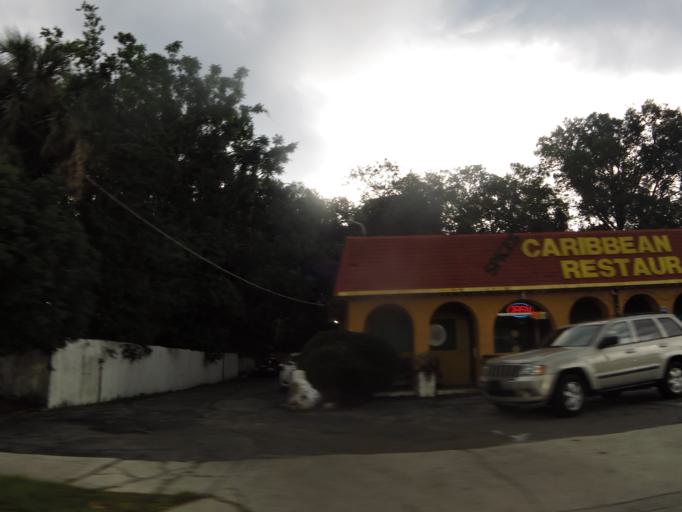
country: US
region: Florida
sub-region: Duval County
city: Jacksonville
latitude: 30.3342
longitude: -81.5891
